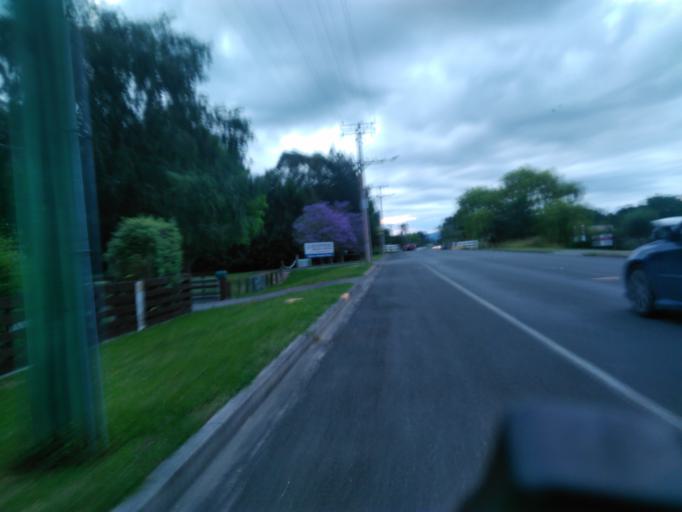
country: NZ
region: Gisborne
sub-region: Gisborne District
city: Gisborne
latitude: -38.6447
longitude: 177.9942
